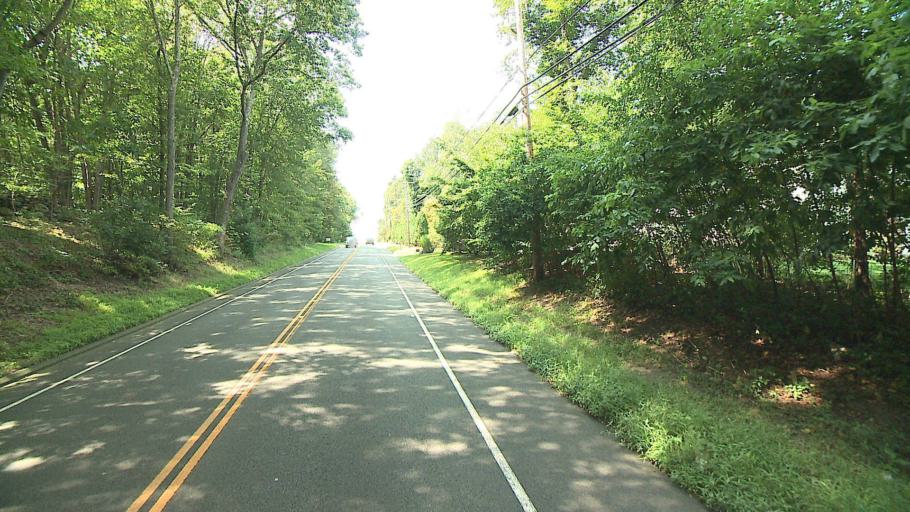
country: US
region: Connecticut
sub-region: Fairfield County
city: Shelton
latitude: 41.3328
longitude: -73.1441
